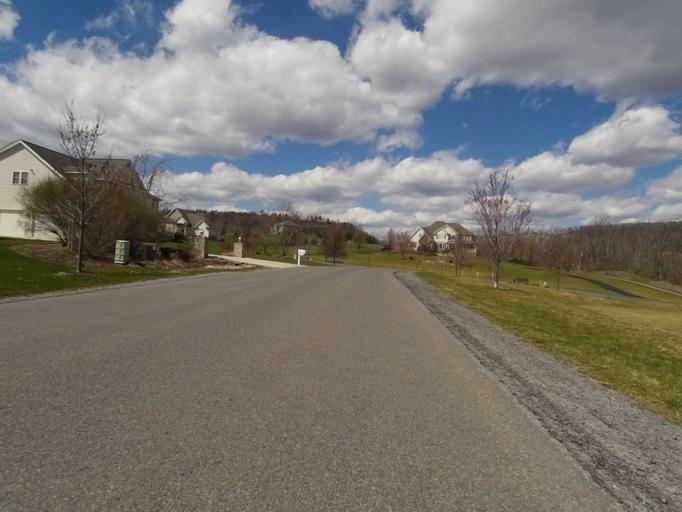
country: US
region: Pennsylvania
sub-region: Centre County
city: Park Forest Village
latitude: 40.8241
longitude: -77.9596
